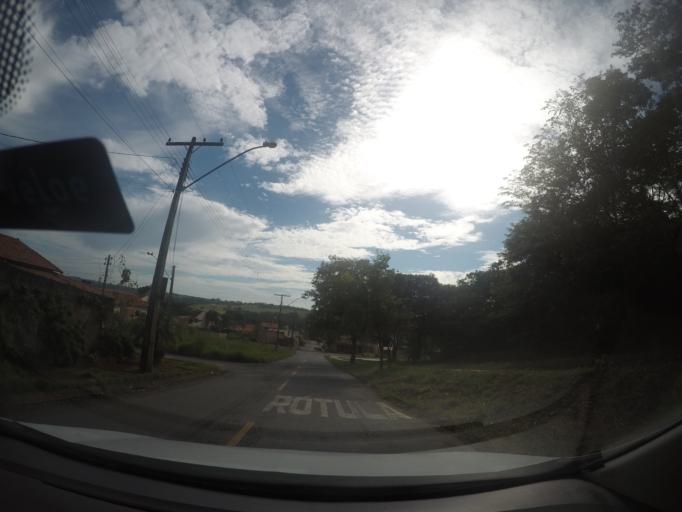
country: BR
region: Goias
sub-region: Goiania
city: Goiania
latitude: -16.6859
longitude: -49.2015
